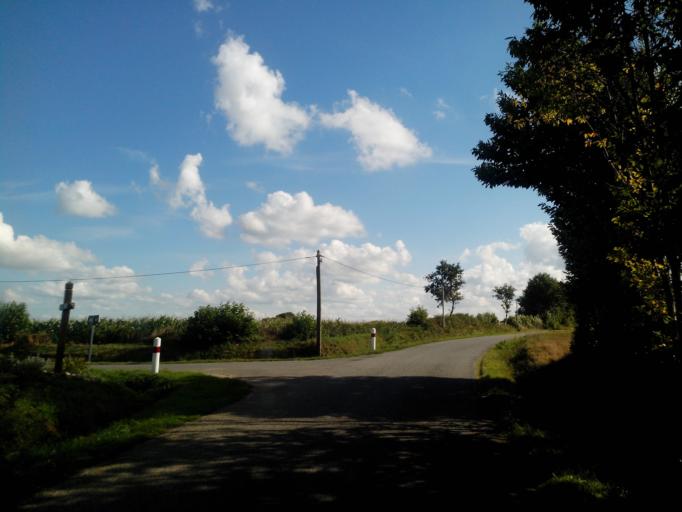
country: FR
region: Brittany
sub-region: Departement des Cotes-d'Armor
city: Merdrignac
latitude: 48.1652
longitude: -2.4180
